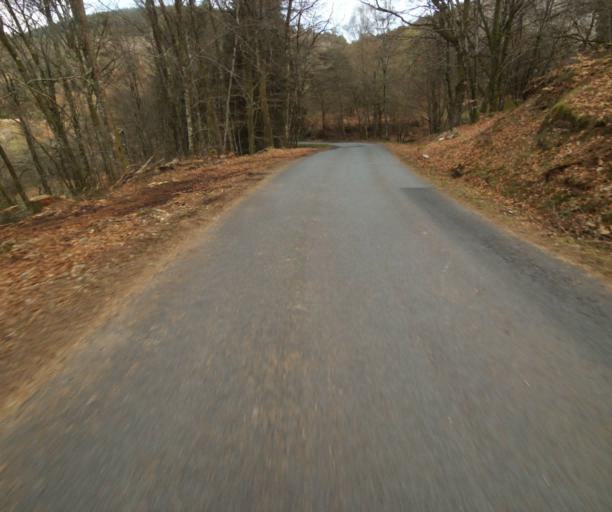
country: FR
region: Limousin
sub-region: Departement de la Correze
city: Correze
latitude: 45.4176
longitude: 1.8985
